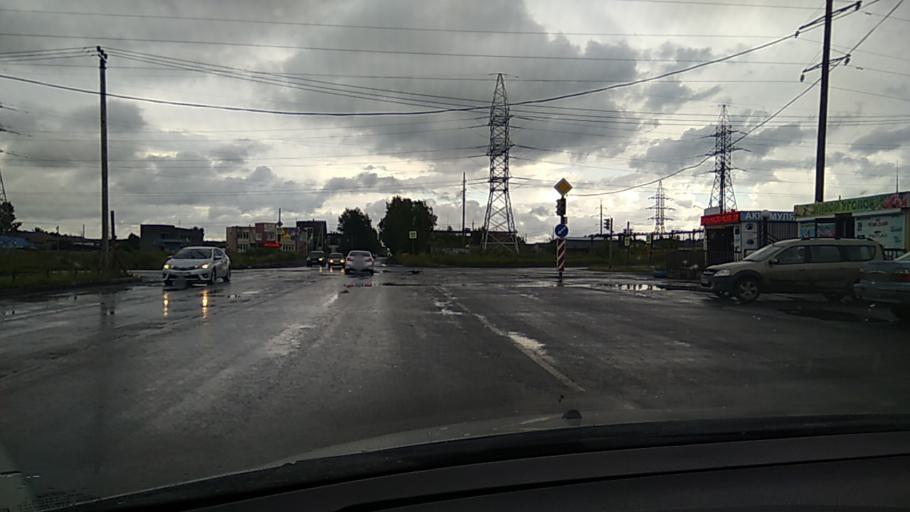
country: RU
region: Sverdlovsk
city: Sredneuralsk
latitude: 56.9917
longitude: 60.4781
